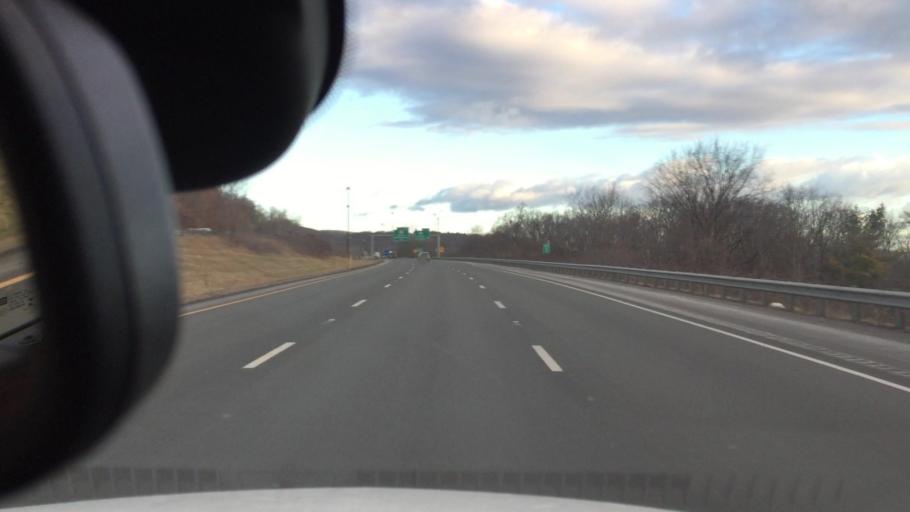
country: US
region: Massachusetts
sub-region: Hampden County
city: Holyoke
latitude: 42.1933
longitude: -72.6377
